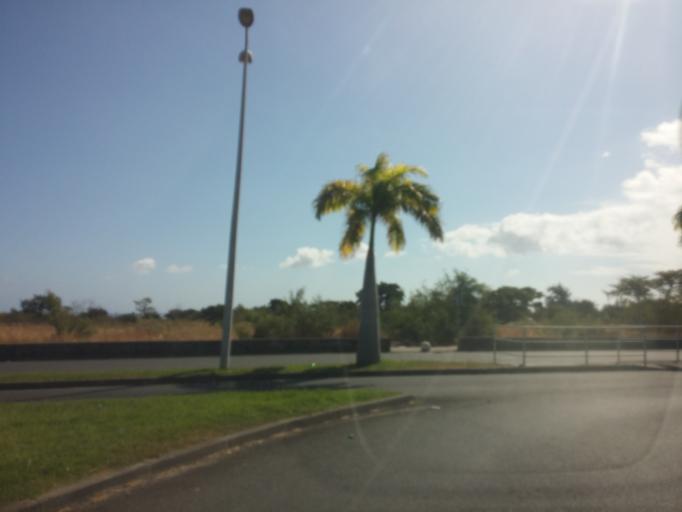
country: RE
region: Reunion
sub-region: Reunion
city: Le Port
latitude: -20.9548
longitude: 55.3080
